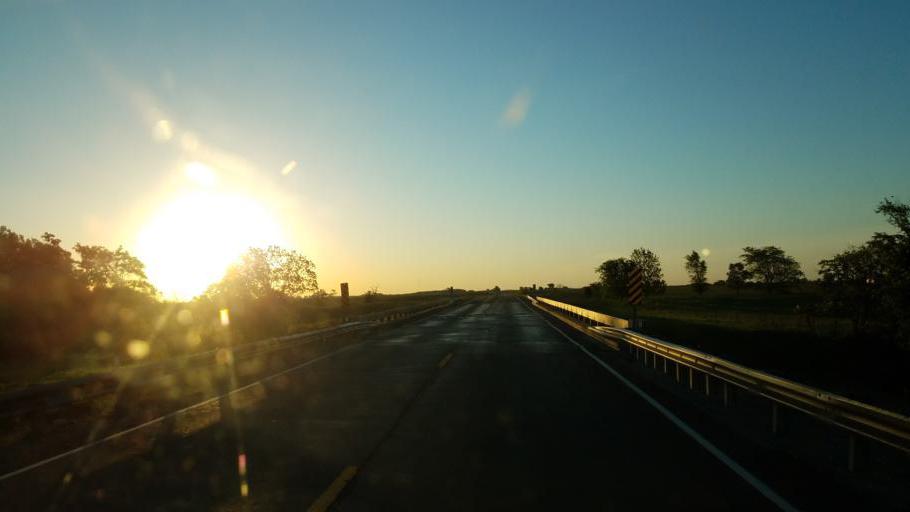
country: US
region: Missouri
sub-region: Schuyler County
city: Lancaster
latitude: 40.4927
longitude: -92.5791
